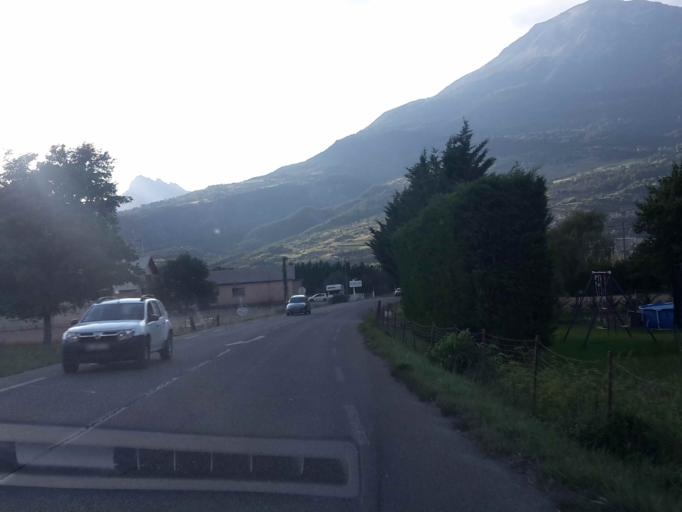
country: FR
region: Provence-Alpes-Cote d'Azur
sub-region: Departement des Hautes-Alpes
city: Embrun
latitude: 44.5441
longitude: 6.4904
